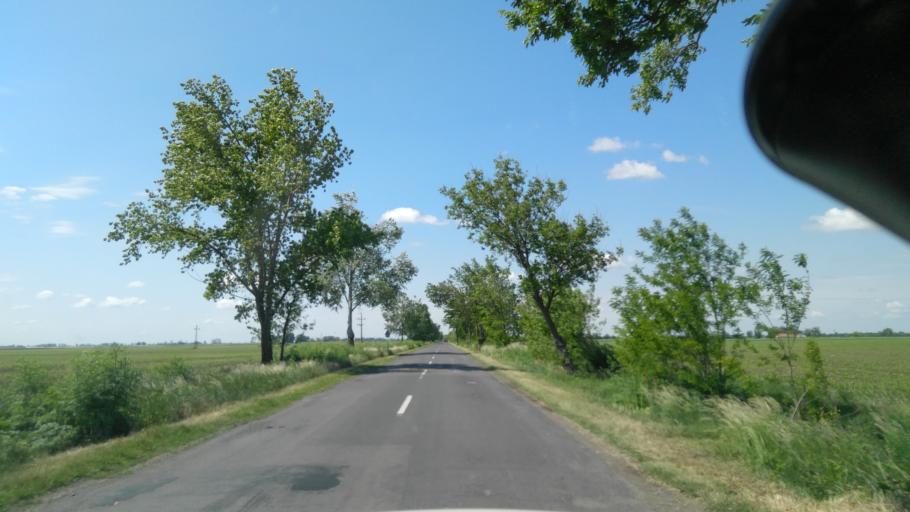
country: HU
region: Bekes
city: Medgyesegyhaza
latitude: 46.4710
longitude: 21.0167
